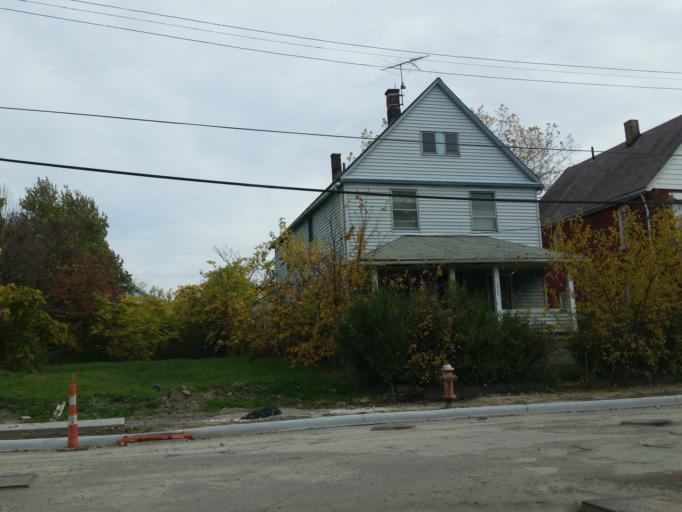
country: US
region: Ohio
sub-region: Cuyahoga County
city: Newburgh Heights
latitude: 41.4776
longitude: -81.6312
